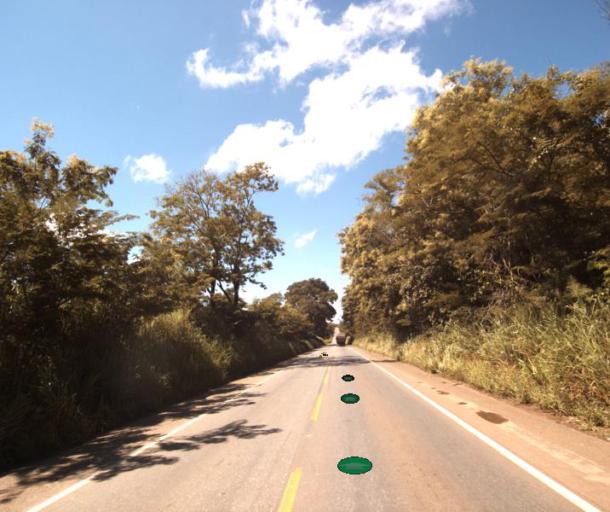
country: BR
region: Goias
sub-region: Jaragua
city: Jaragua
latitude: -15.6736
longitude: -49.3471
